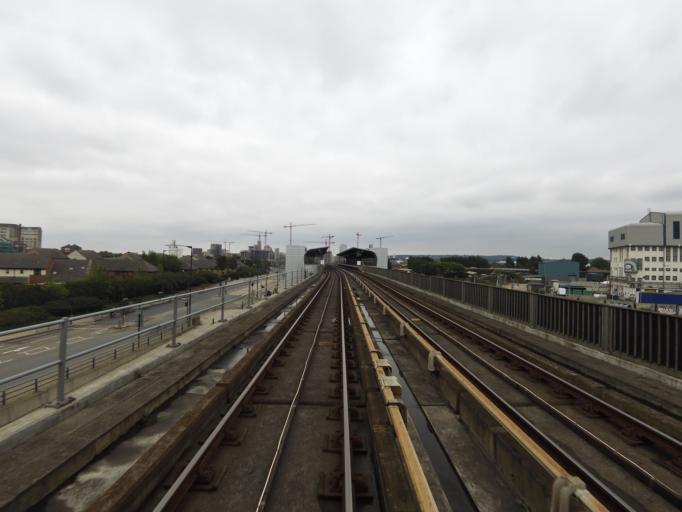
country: GB
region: England
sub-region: Greater London
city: Poplar
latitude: 51.5028
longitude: 0.0228
